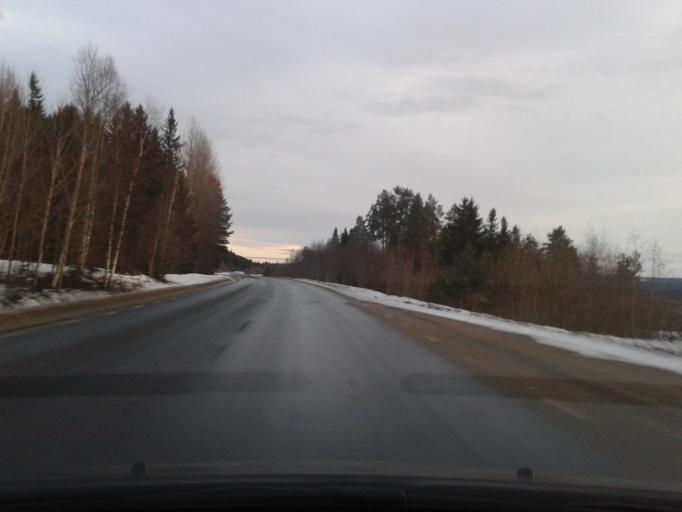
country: SE
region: Vaesternorrland
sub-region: Solleftea Kommun
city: Solleftea
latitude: 63.2193
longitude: 17.2227
